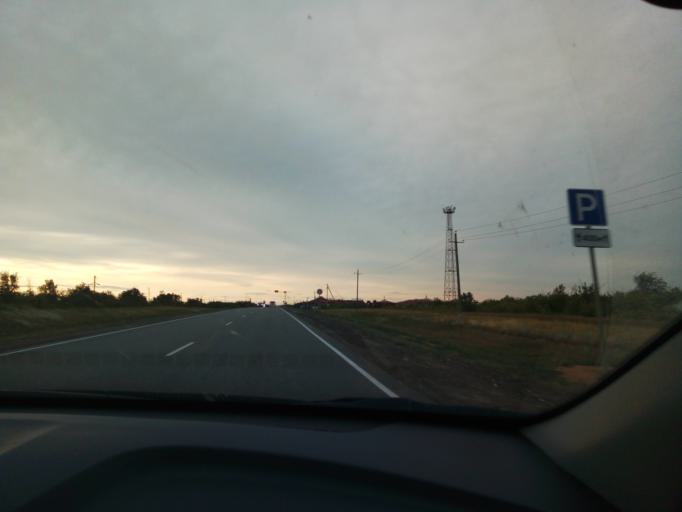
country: RU
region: Volgograd
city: Primorsk
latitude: 49.2626
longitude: 44.8816
